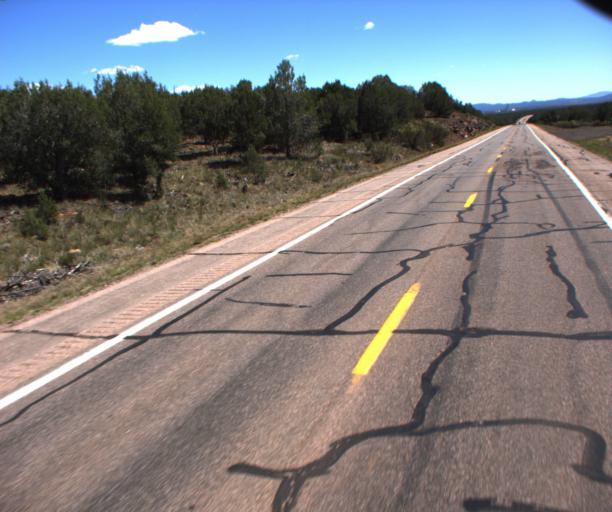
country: US
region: Arizona
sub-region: Yavapai County
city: Paulden
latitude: 35.0613
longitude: -112.3991
